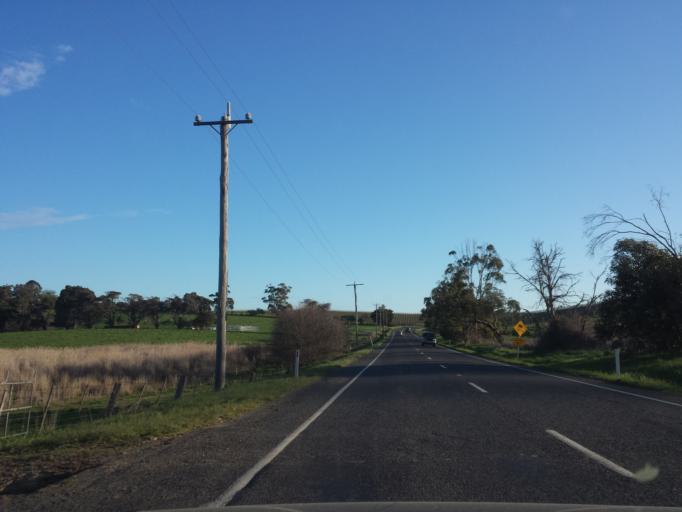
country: AU
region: Victoria
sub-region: Yarra Ranges
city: Yarra Glen
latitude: -37.6290
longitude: 145.4074
